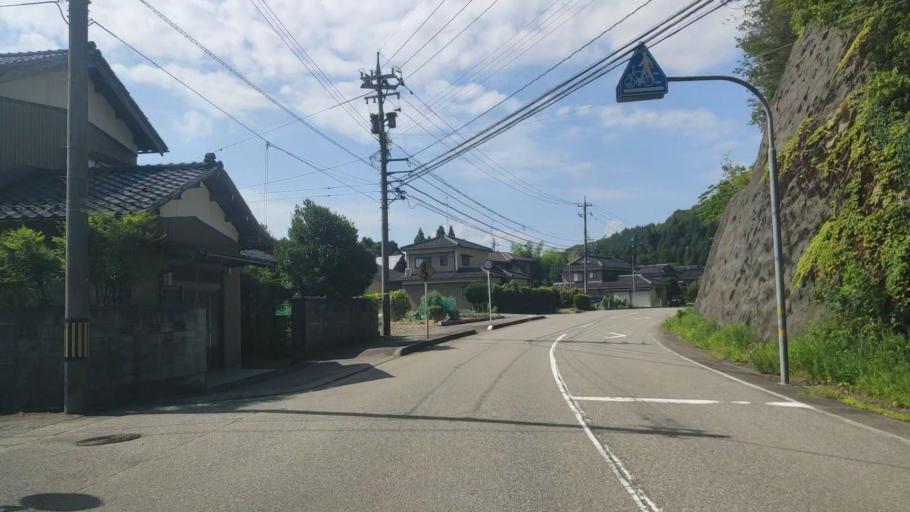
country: JP
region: Ishikawa
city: Komatsu
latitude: 36.3608
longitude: 136.4938
